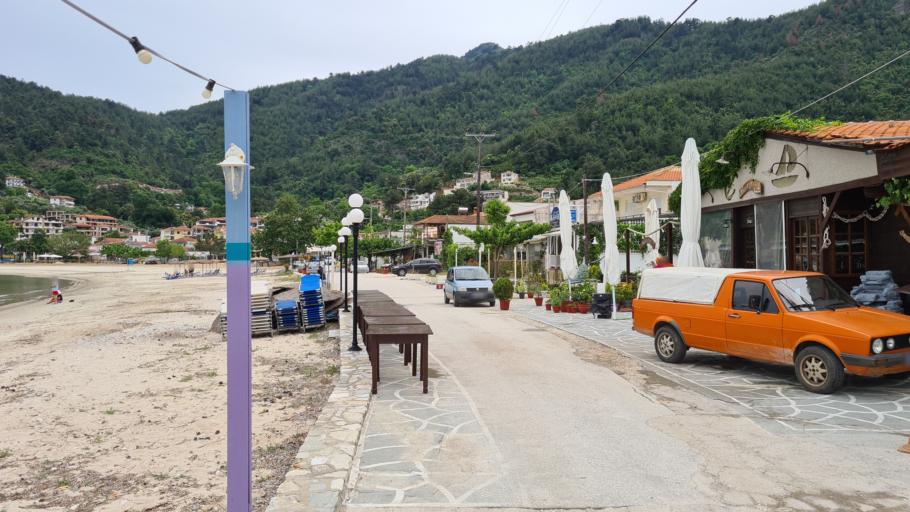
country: GR
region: East Macedonia and Thrace
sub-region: Nomos Kavalas
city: Potamia
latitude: 40.7104
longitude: 24.7592
